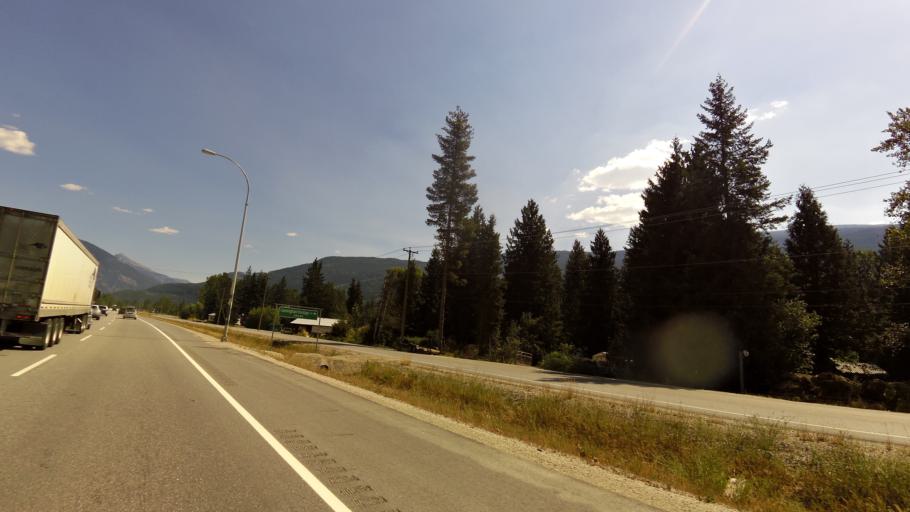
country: CA
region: British Columbia
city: Sicamous
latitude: 50.9538
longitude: -118.7591
